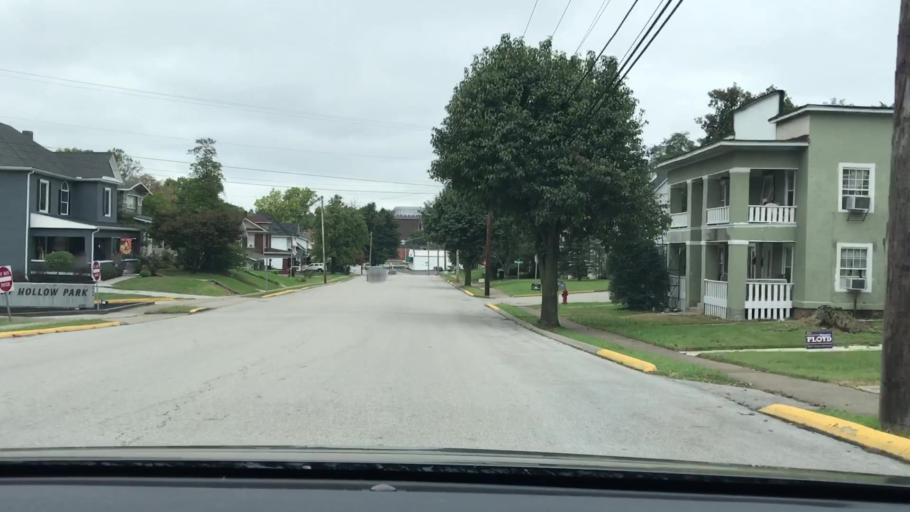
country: US
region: Kentucky
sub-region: Pulaski County
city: Somerset
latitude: 37.0892
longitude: -84.5999
